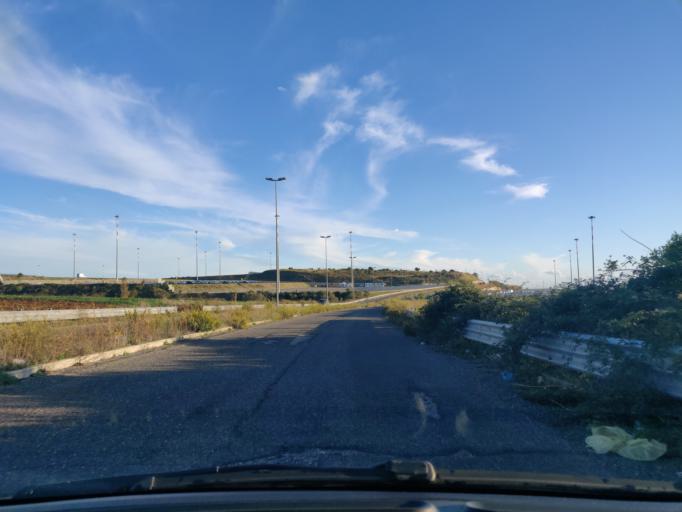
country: IT
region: Latium
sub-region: Citta metropolitana di Roma Capitale
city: Aurelia
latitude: 42.1305
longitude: 11.7773
